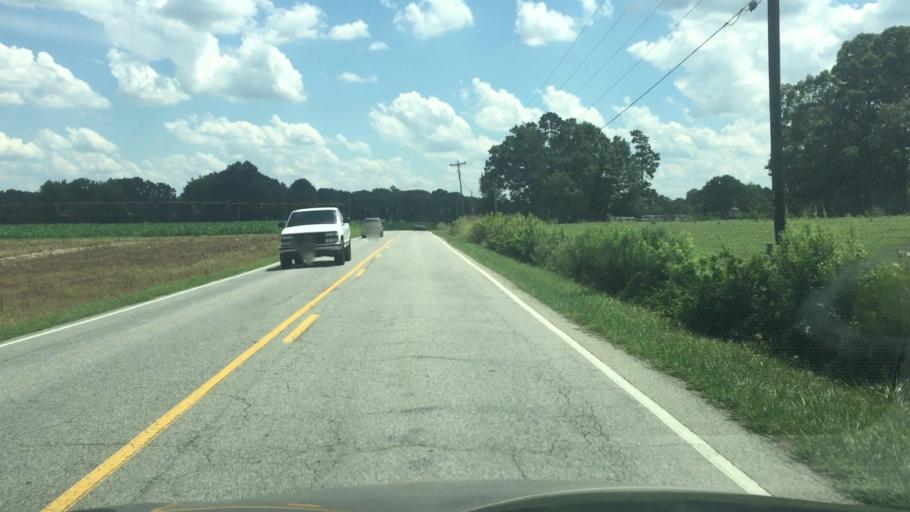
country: US
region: North Carolina
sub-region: Rowan County
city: Enochville
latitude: 35.5735
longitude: -80.6544
